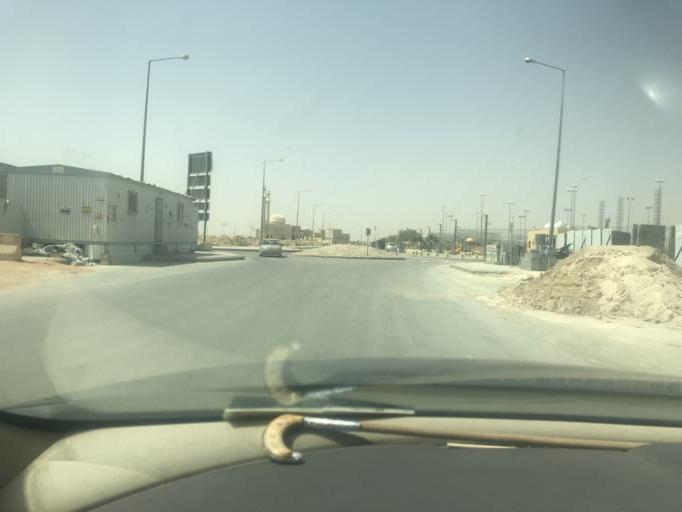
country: SA
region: Ar Riyad
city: Riyadh
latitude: 24.7874
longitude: 46.5808
